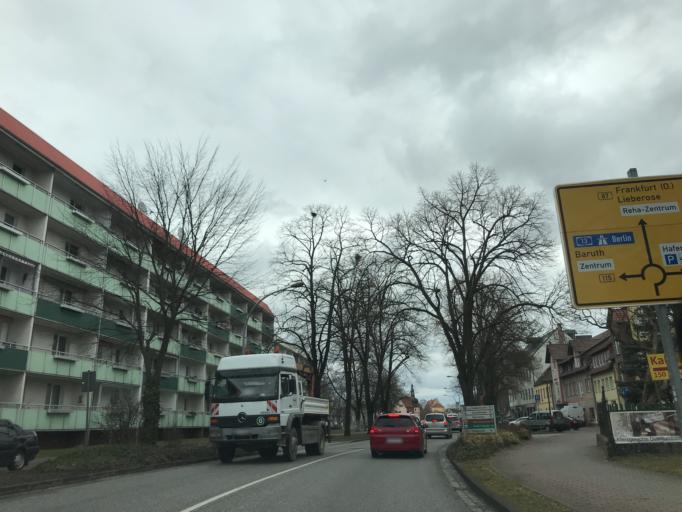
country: DE
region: Brandenburg
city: Luebben
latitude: 51.9392
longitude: 13.8915
